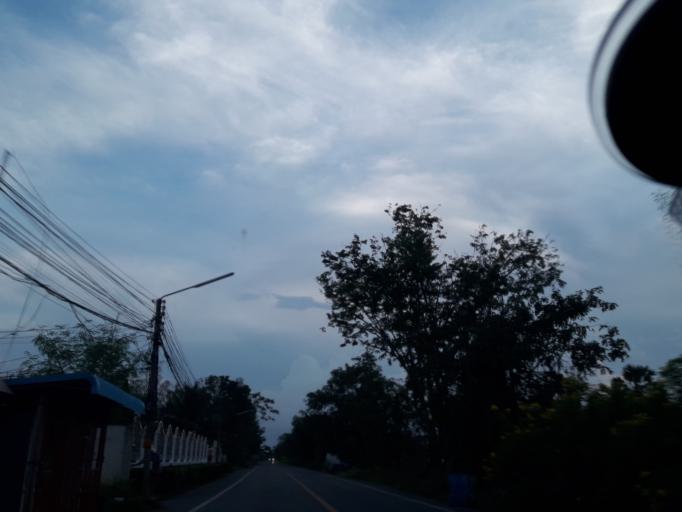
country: TH
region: Pathum Thani
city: Nong Suea
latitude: 14.1253
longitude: 100.8690
